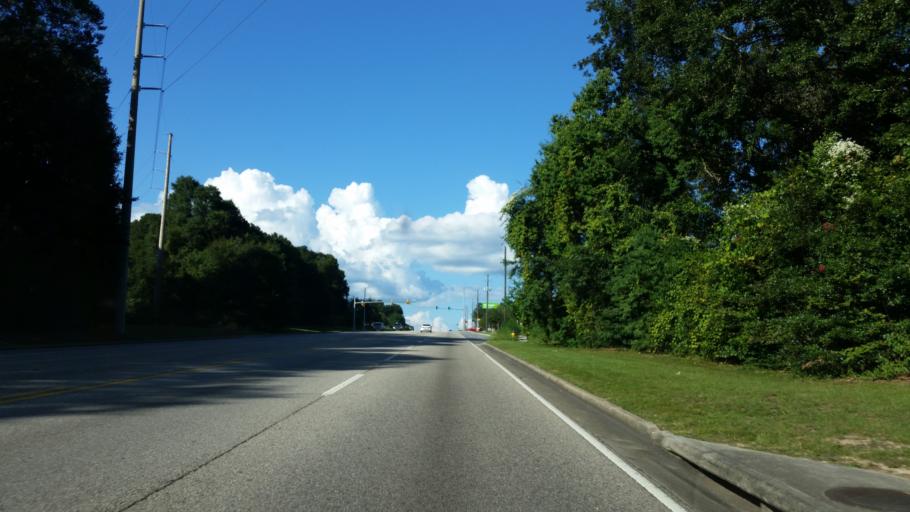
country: US
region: Alabama
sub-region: Mobile County
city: Prichard
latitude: 30.7157
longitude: -88.1657
